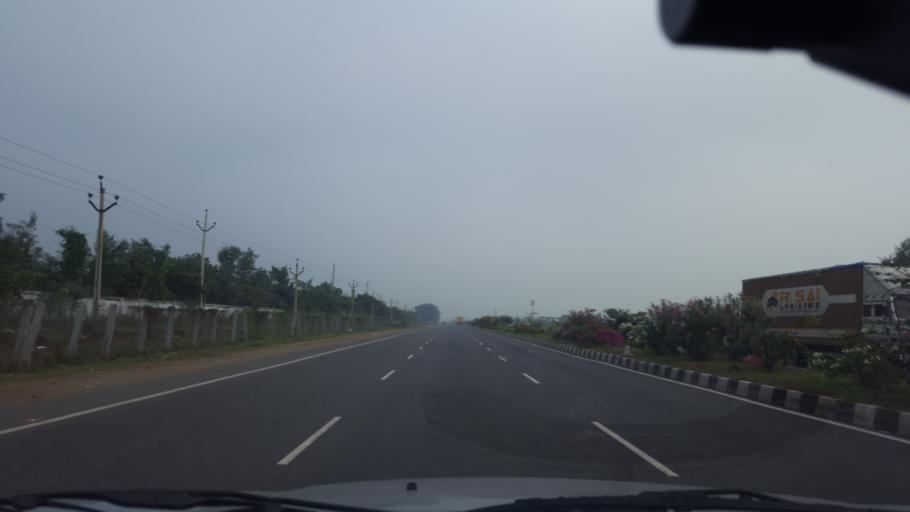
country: IN
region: Andhra Pradesh
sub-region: Prakasam
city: Addanki
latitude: 15.6665
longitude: 80.0156
